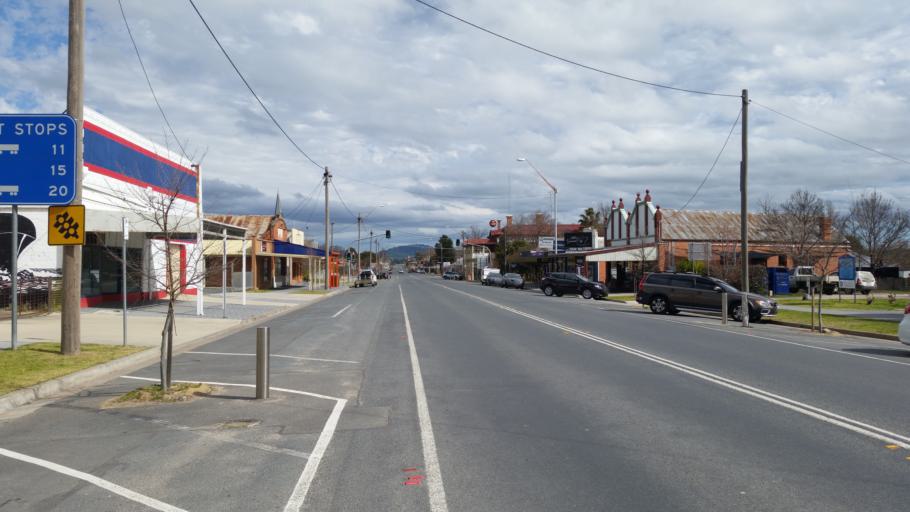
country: AU
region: New South Wales
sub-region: Greater Hume Shire
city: Holbrook
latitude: -35.7213
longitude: 147.3157
